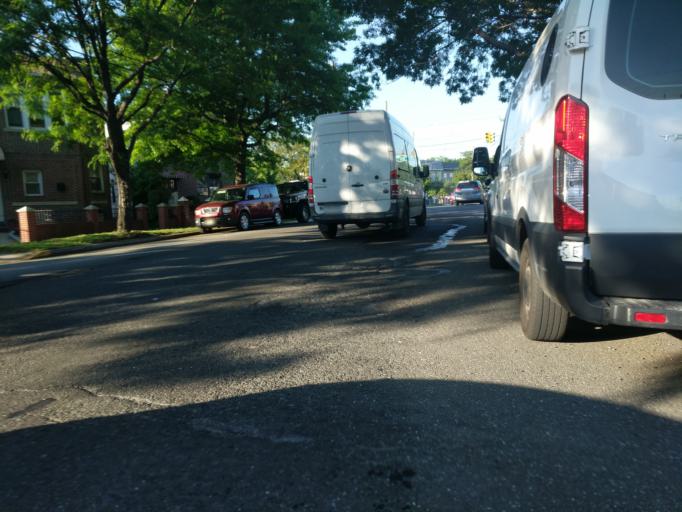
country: US
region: New York
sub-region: Queens County
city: Long Island City
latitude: 40.7346
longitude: -73.9004
